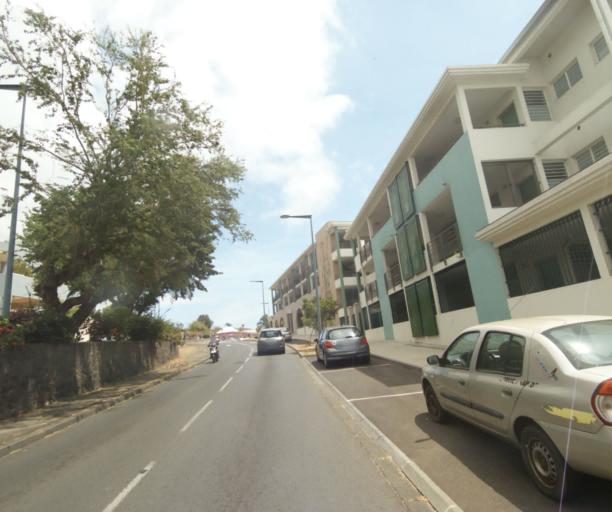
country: RE
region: Reunion
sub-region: Reunion
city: Saint-Paul
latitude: -21.0256
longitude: 55.2658
